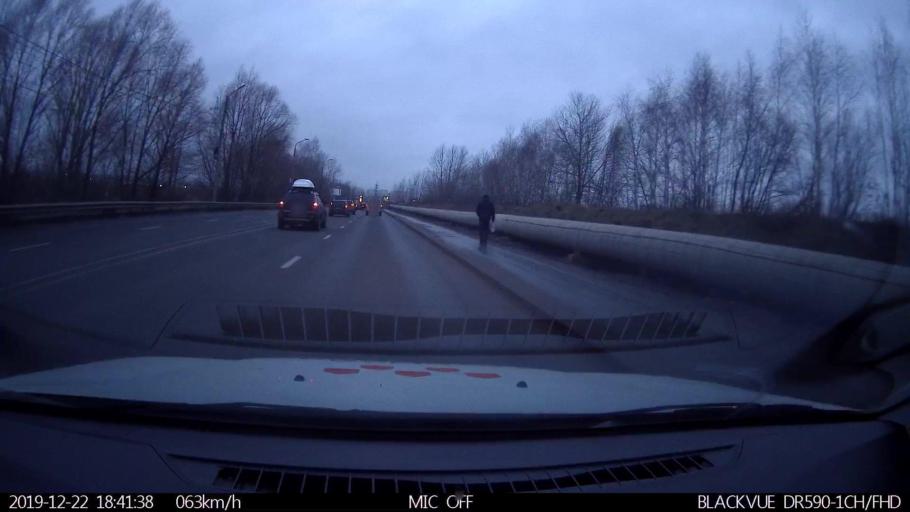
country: RU
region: Nizjnij Novgorod
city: Nizhniy Novgorod
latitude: 56.3425
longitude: 43.9021
